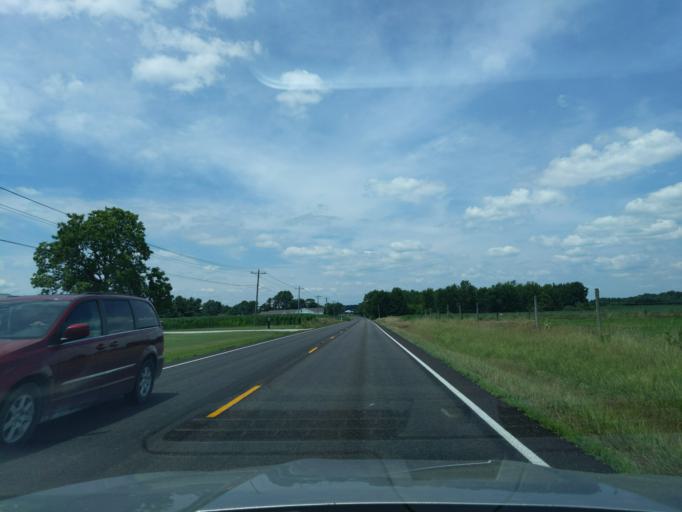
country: US
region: Indiana
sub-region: Ripley County
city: Osgood
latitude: 39.2386
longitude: -85.3440
